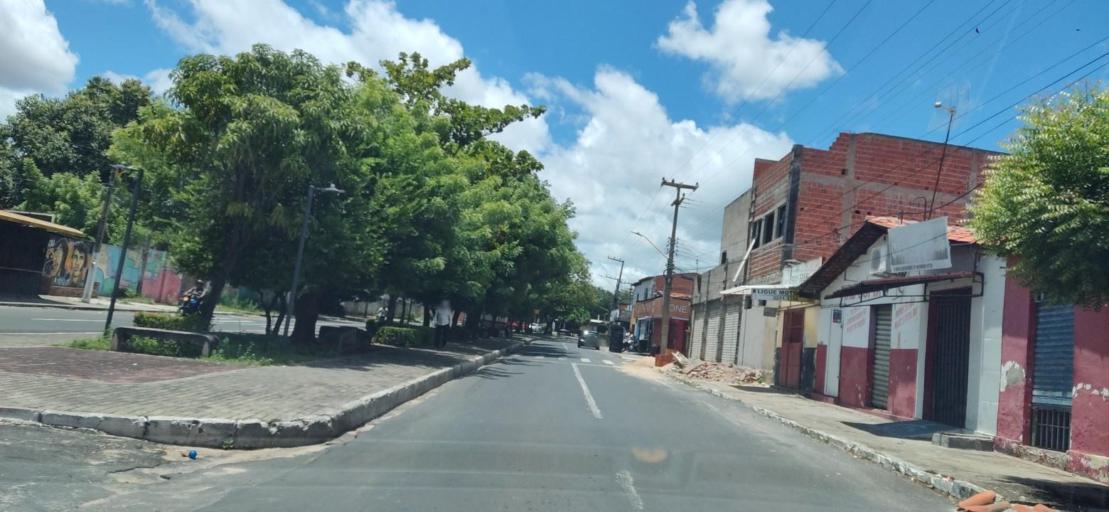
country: BR
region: Piaui
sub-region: Teresina
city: Teresina
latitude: -5.1487
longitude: -42.7818
